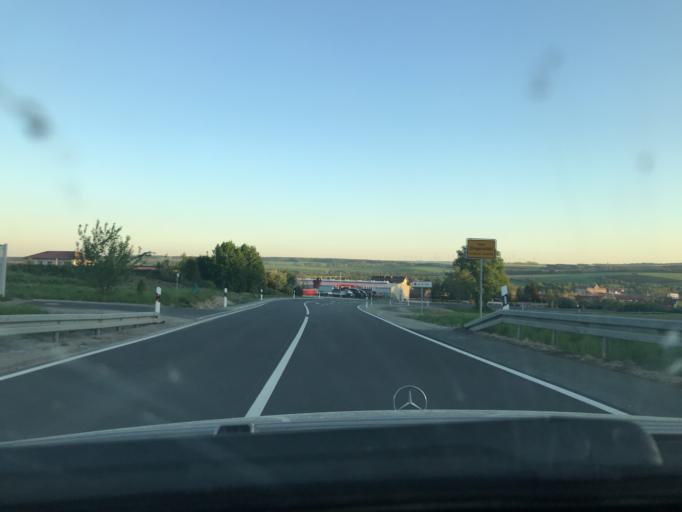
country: DE
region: Thuringia
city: Dingelstadt
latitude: 51.3265
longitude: 10.3224
